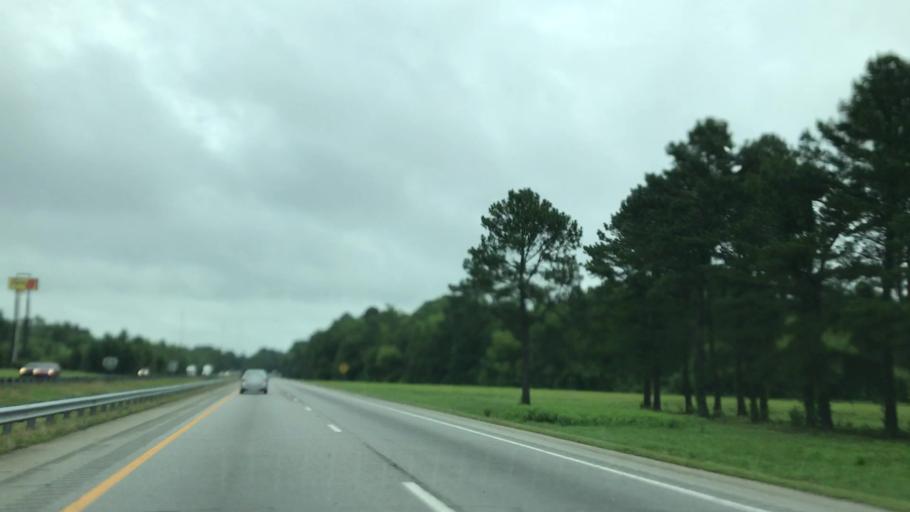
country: US
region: North Carolina
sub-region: Halifax County
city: Roanoke Rapids
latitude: 36.4688
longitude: -77.6111
